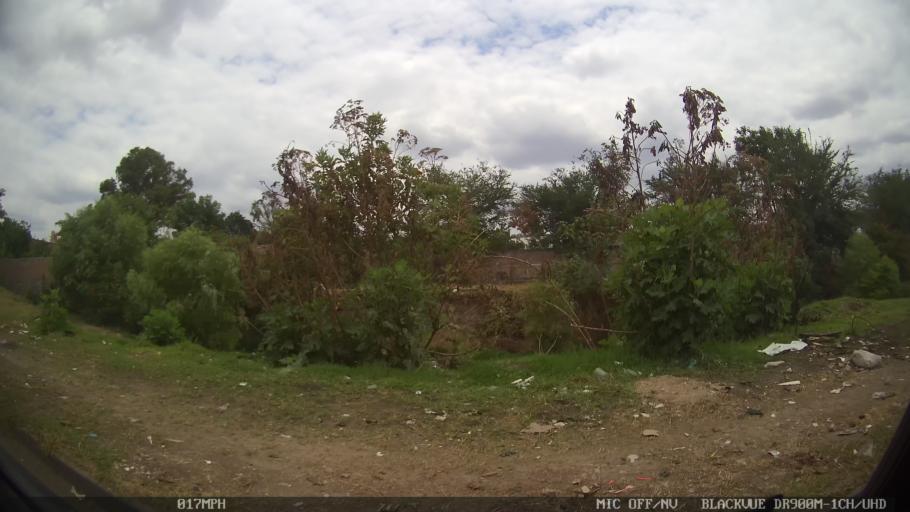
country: MX
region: Jalisco
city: Tlaquepaque
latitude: 20.6449
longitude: -103.2742
